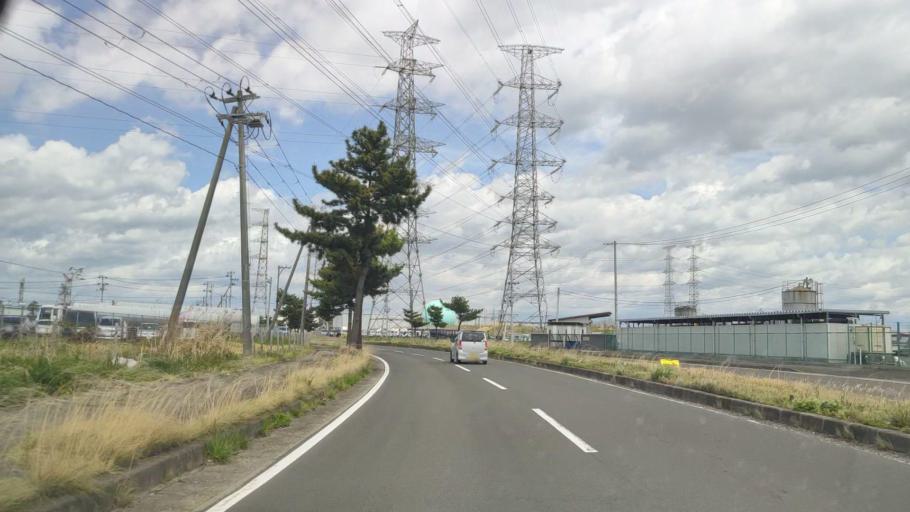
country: JP
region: Miyagi
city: Shiogama
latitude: 38.2825
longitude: 141.0246
